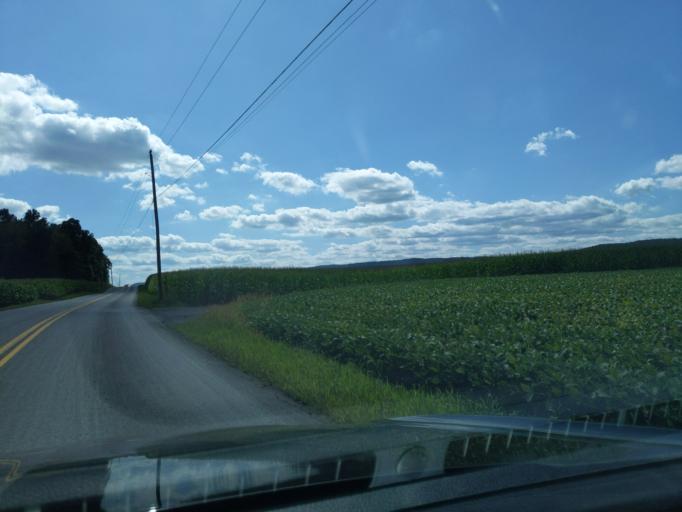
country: US
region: Pennsylvania
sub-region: Blair County
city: Tyrone
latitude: 40.6354
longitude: -78.2239
